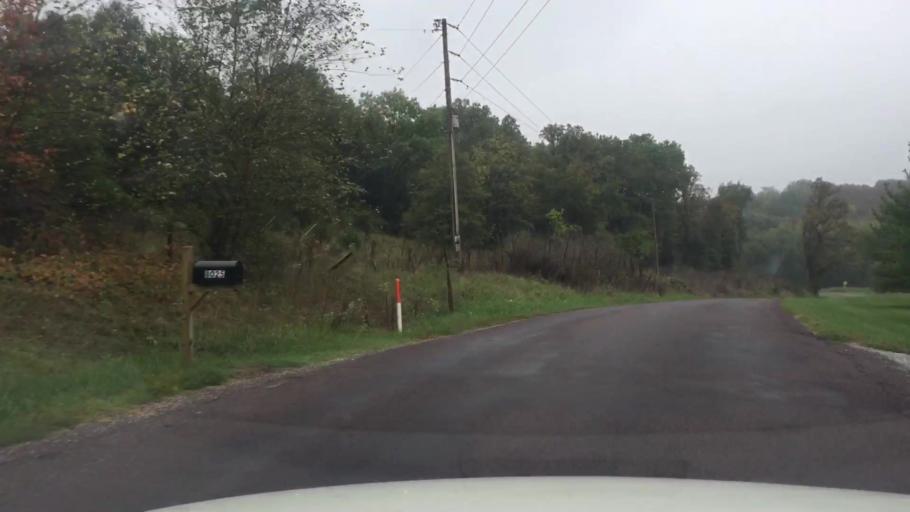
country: US
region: Missouri
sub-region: Boone County
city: Columbia
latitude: 38.8588
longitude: -92.3727
